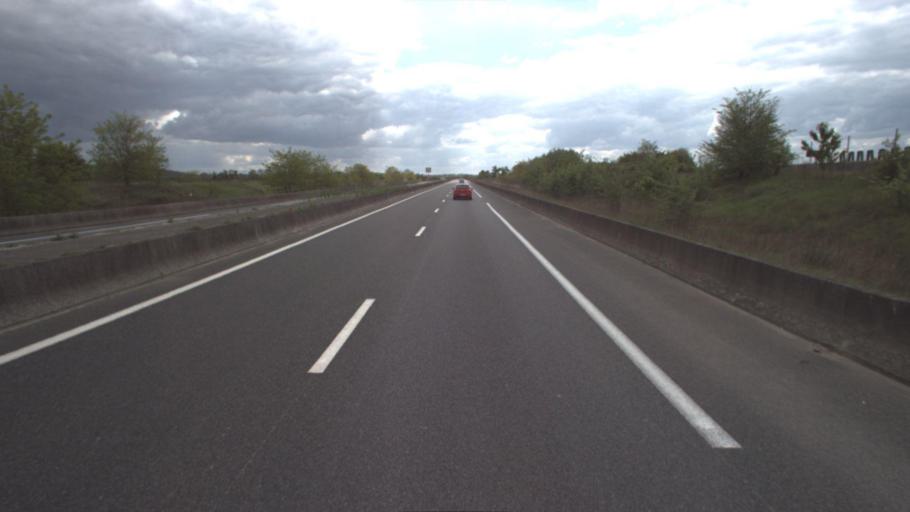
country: FR
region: Ile-de-France
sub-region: Departement de Seine-et-Marne
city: Mareuil-les-Meaux
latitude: 48.9306
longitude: 2.8456
